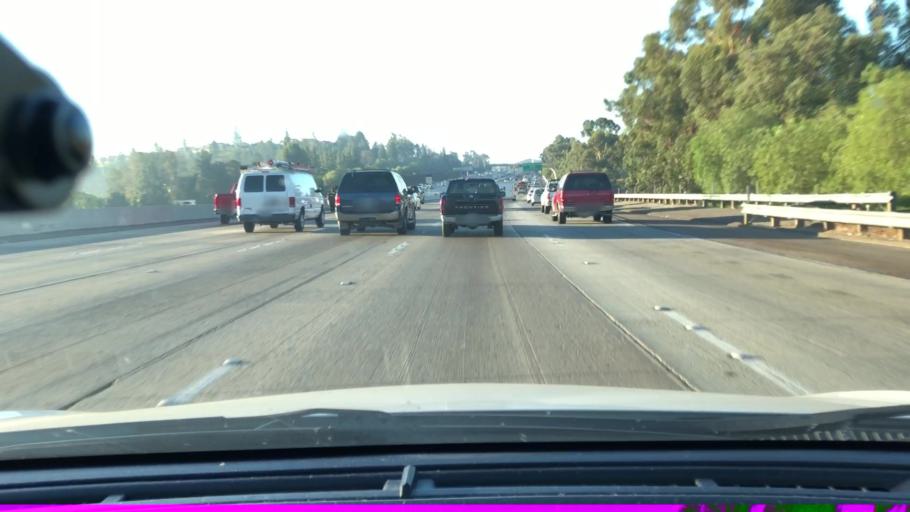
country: US
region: California
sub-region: San Diego County
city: Escondido
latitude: 33.0443
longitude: -117.0736
